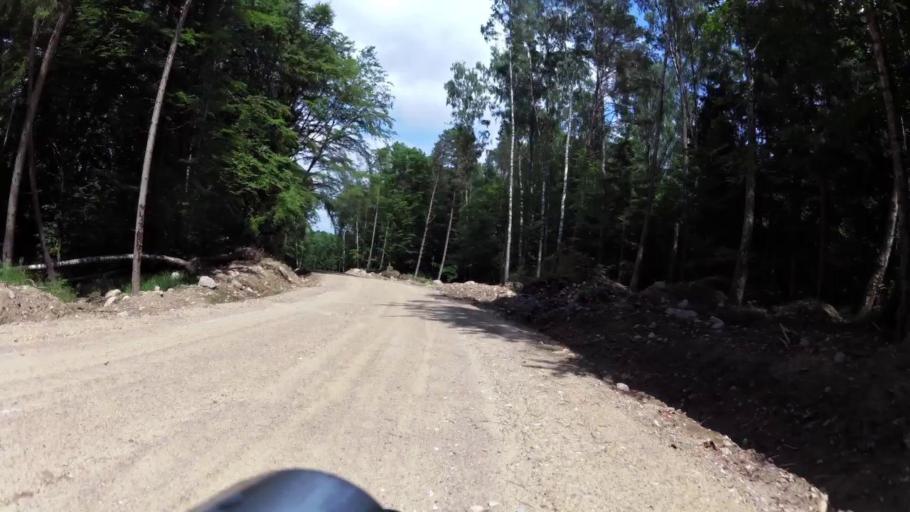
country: PL
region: West Pomeranian Voivodeship
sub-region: Powiat szczecinecki
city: Bialy Bor
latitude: 53.9631
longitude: 16.7579
